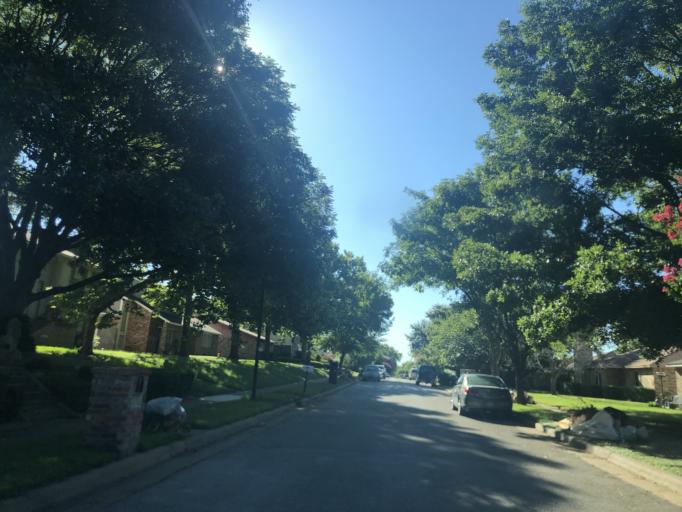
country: US
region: Texas
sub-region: Dallas County
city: Duncanville
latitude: 32.6451
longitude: -96.9507
